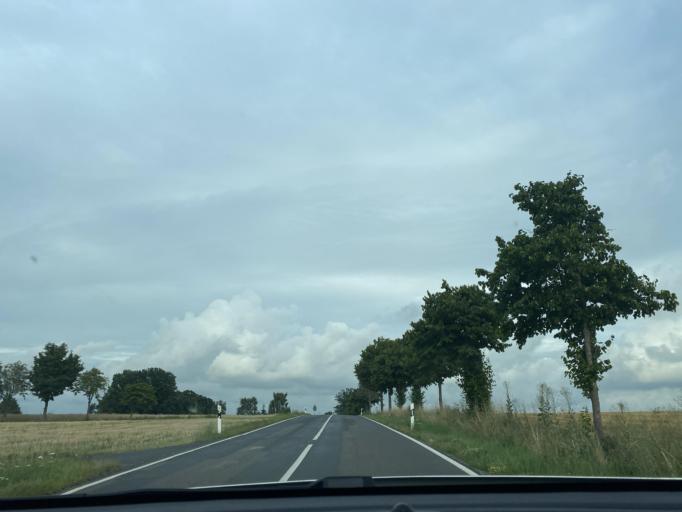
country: DE
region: Saxony
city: Grosshennersdorf
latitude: 51.0186
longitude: 14.7952
